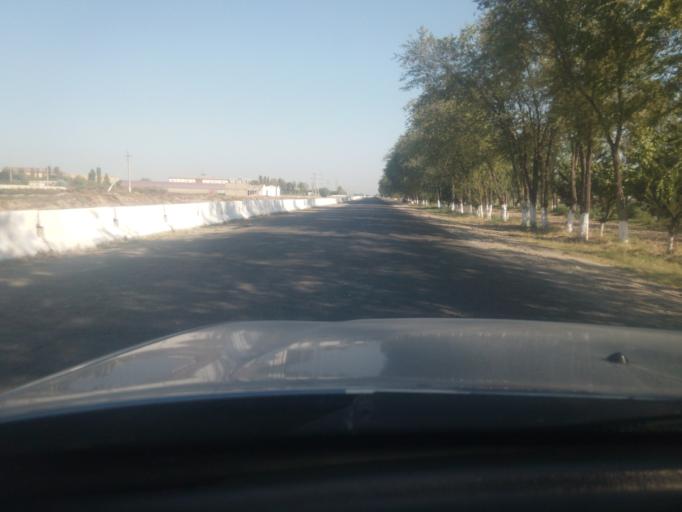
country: UZ
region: Sirdaryo
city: Guliston
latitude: 40.5126
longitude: 68.7947
